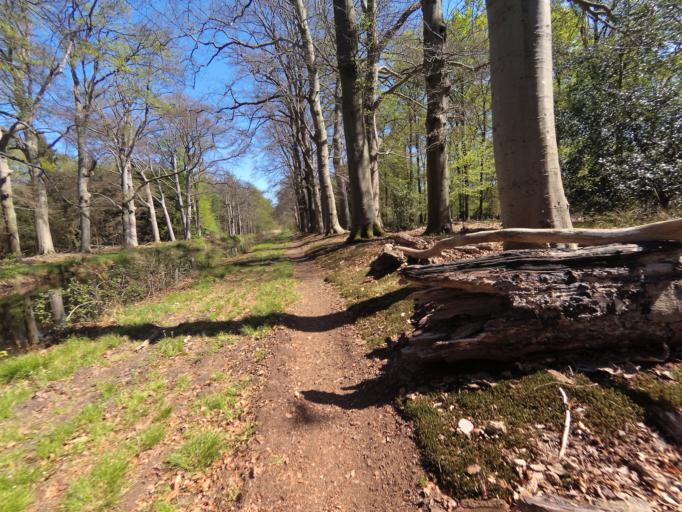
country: NL
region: Utrecht
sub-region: Gemeente Woudenberg
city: Woudenberg
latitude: 52.0893
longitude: 5.4047
